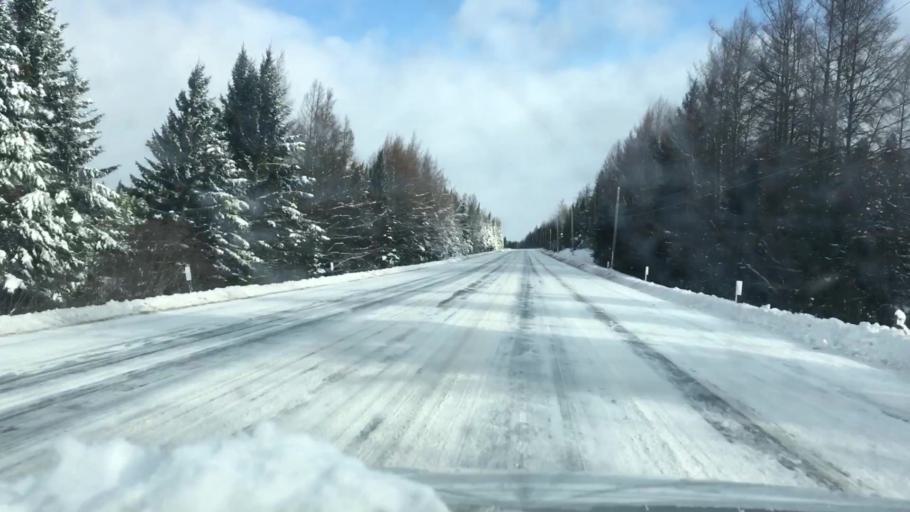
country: US
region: Maine
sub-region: Aroostook County
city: Van Buren
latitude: 47.0612
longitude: -67.9908
